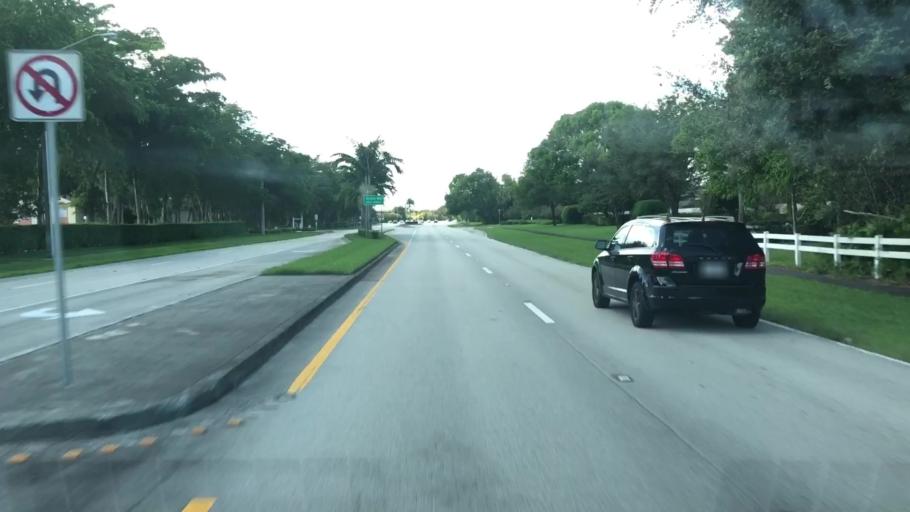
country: US
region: Florida
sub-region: Broward County
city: Coral Springs
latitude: 26.2449
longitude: -80.2690
